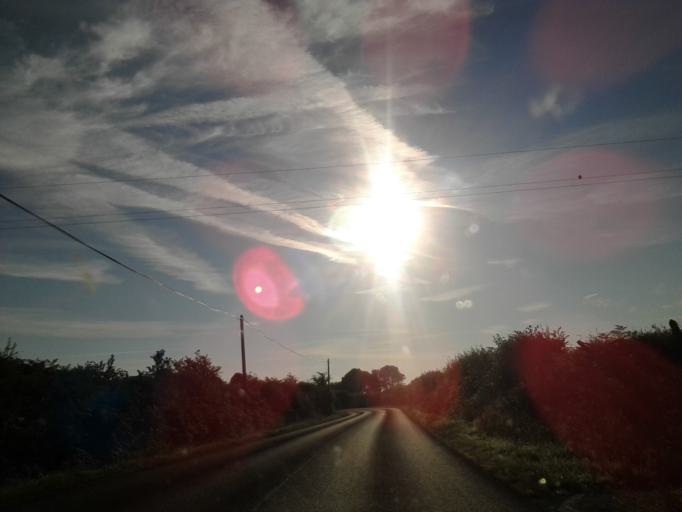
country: FR
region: Lower Normandy
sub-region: Departement de la Manche
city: Digosville
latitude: 49.6009
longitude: -1.4747
